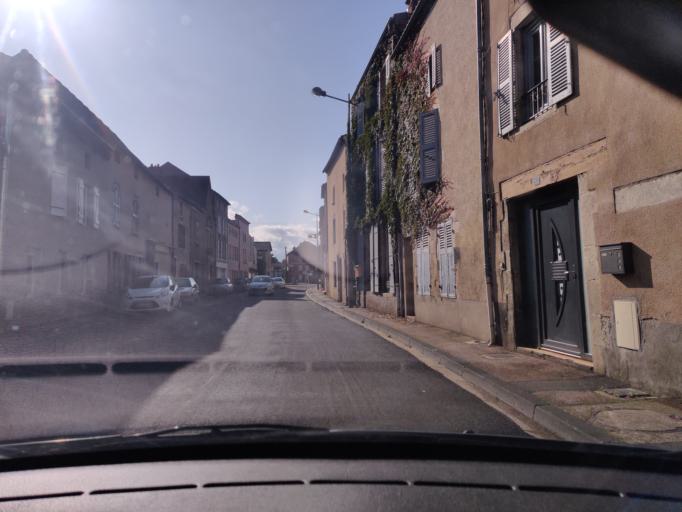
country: FR
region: Auvergne
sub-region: Departement du Puy-de-Dome
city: Aigueperse
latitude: 46.0192
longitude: 3.2009
